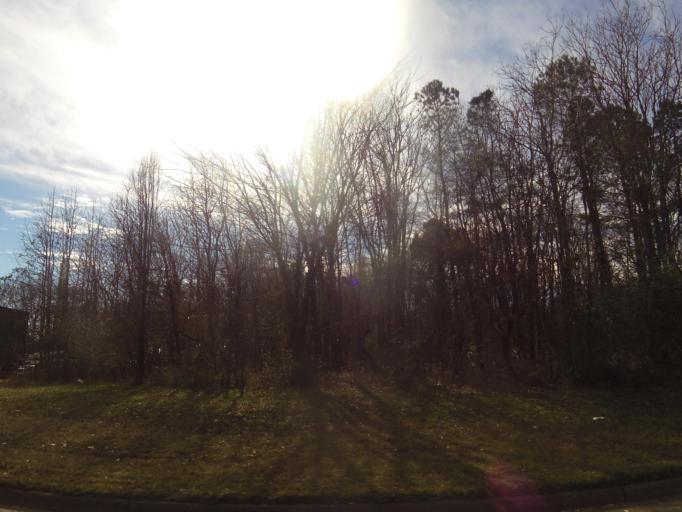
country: US
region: Virginia
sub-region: City of Hopewell
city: Hopewell
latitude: 37.2936
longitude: -77.2846
